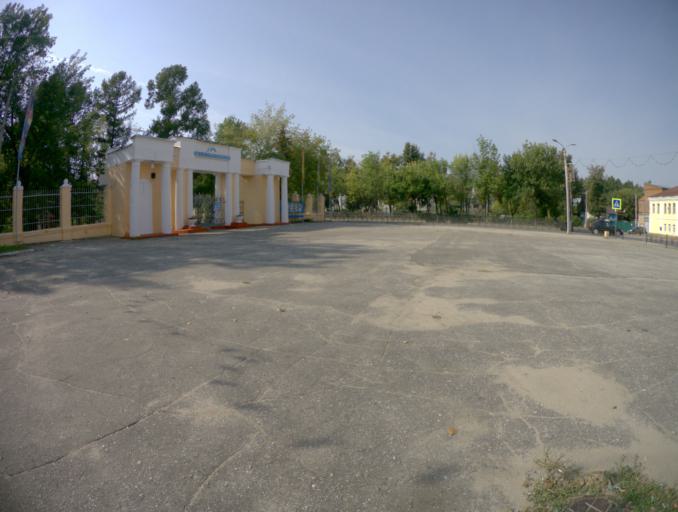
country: RU
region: Vladimir
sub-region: Kovrovskiy Rayon
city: Kovrov
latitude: 56.3743
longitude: 41.3076
